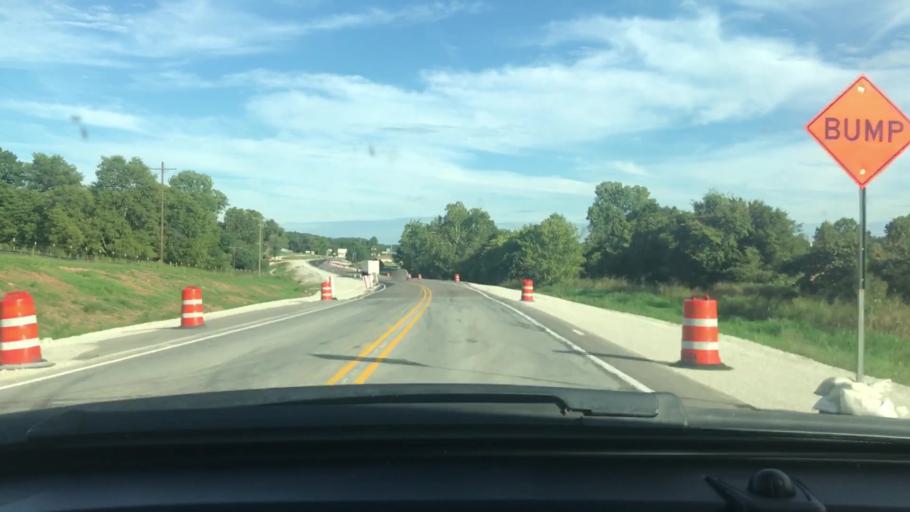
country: US
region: Arkansas
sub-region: Sharp County
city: Cherokee Village
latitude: 36.3048
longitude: -91.4504
